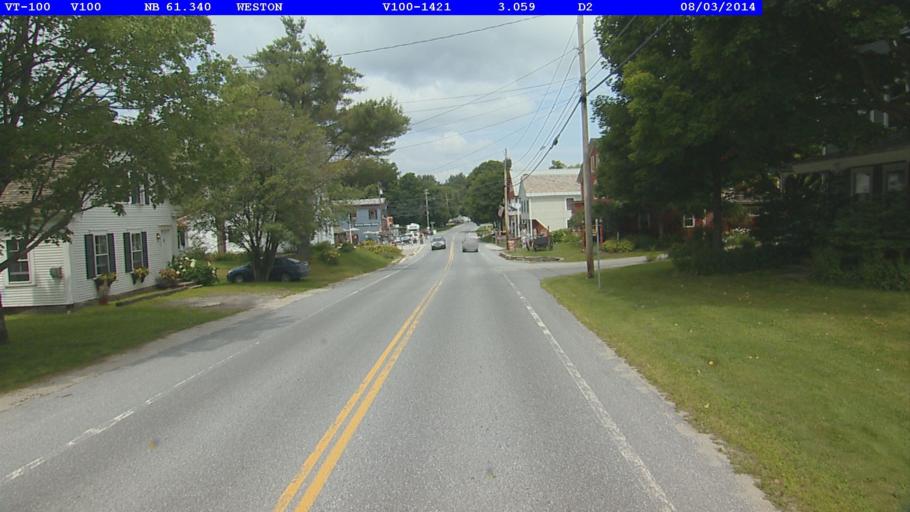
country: US
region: Vermont
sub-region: Windsor County
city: Chester
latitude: 43.2899
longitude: -72.7930
